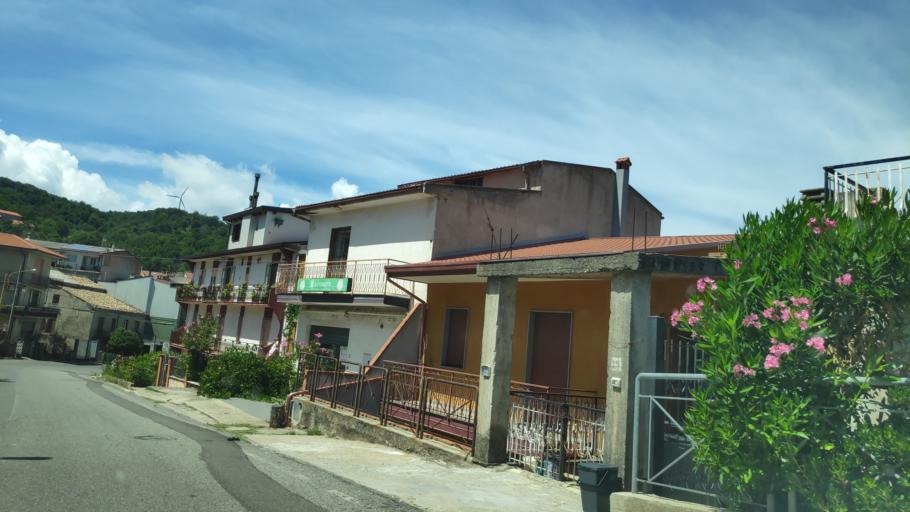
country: IT
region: Calabria
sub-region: Provincia di Catanzaro
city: Palermiti
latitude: 38.7488
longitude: 16.4548
